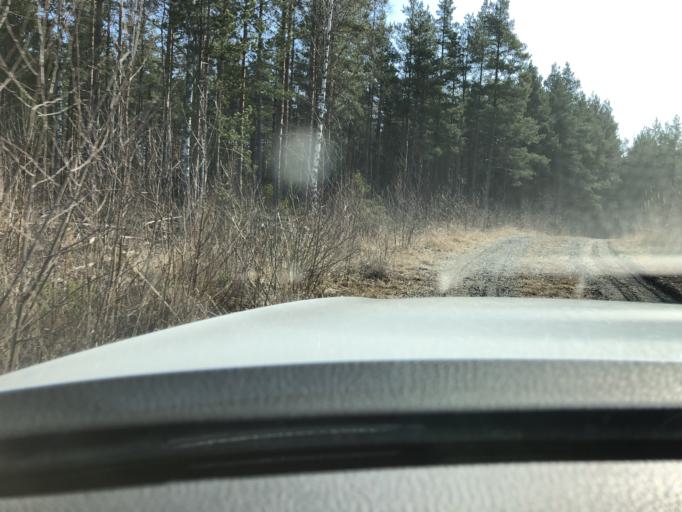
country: SE
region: Uppsala
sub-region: Heby Kommun
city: OEstervala
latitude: 60.3349
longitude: 17.1701
